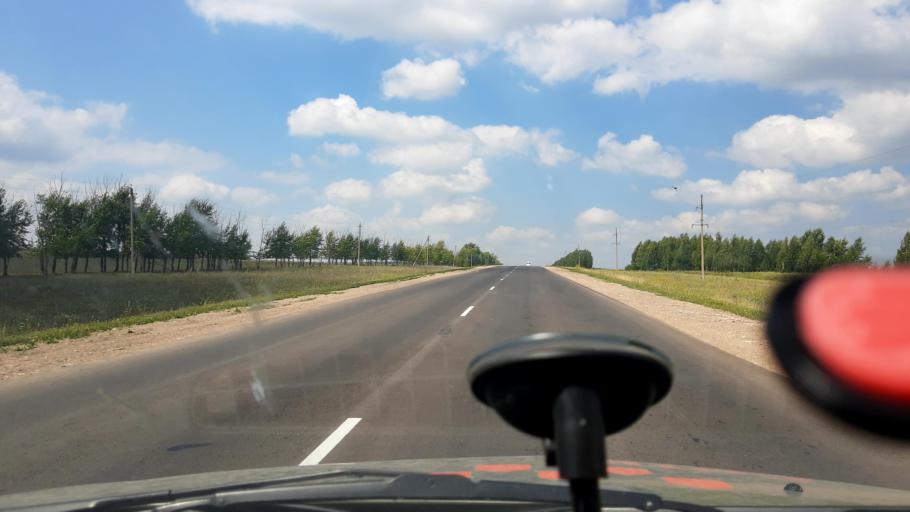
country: RU
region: Bashkortostan
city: Chekmagush
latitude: 54.9099
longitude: 54.5860
